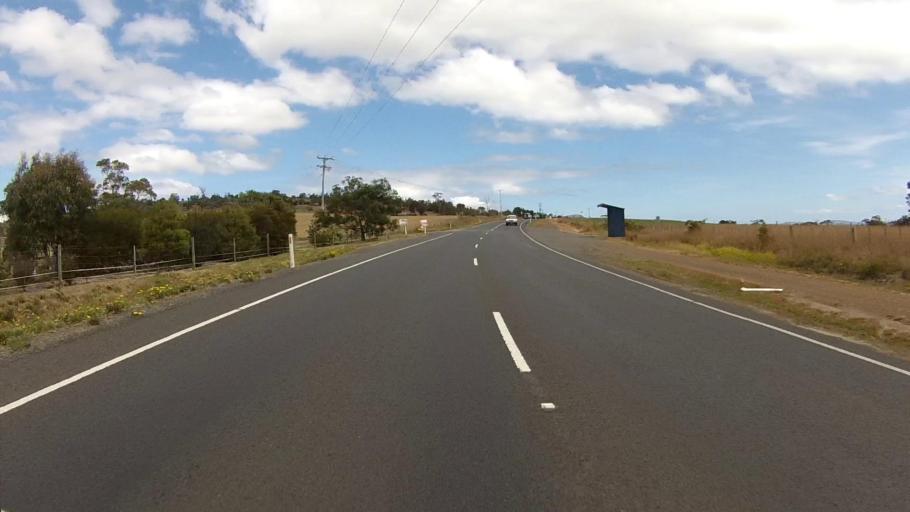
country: AU
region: Tasmania
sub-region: Sorell
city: Sorell
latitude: -42.8326
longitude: 147.6246
